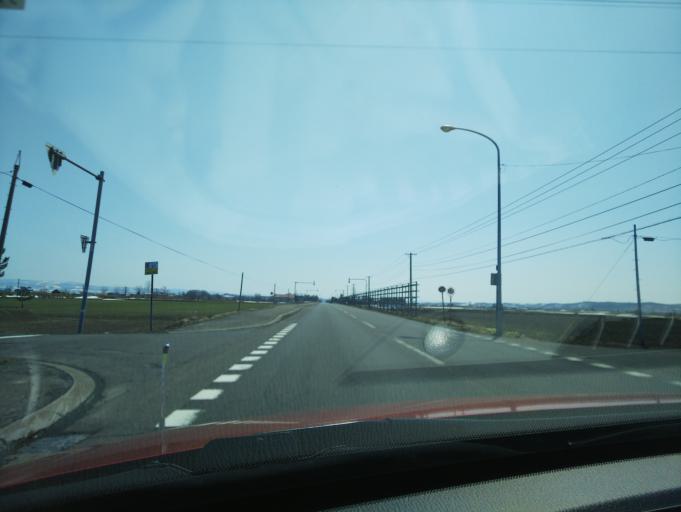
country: JP
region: Hokkaido
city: Nayoro
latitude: 44.2310
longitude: 142.3948
